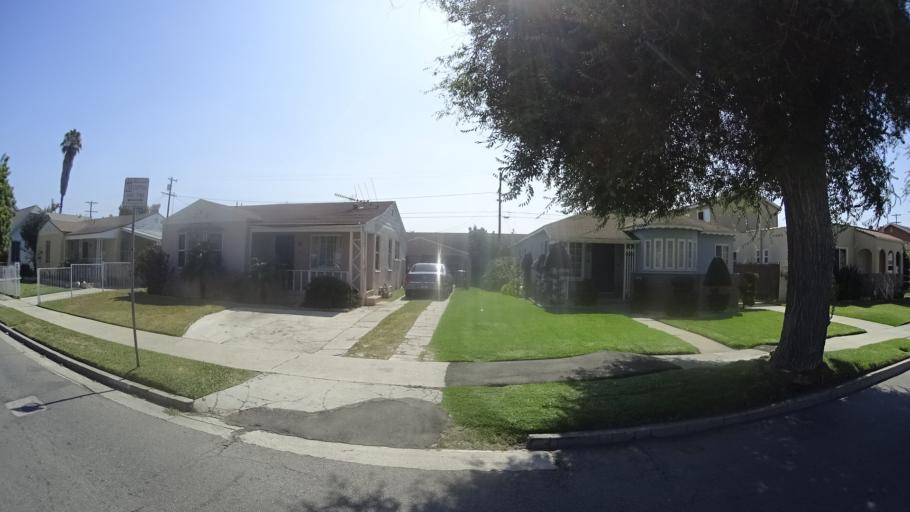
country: US
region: California
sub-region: Los Angeles County
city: View Park-Windsor Hills
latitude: 33.9869
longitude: -118.3149
